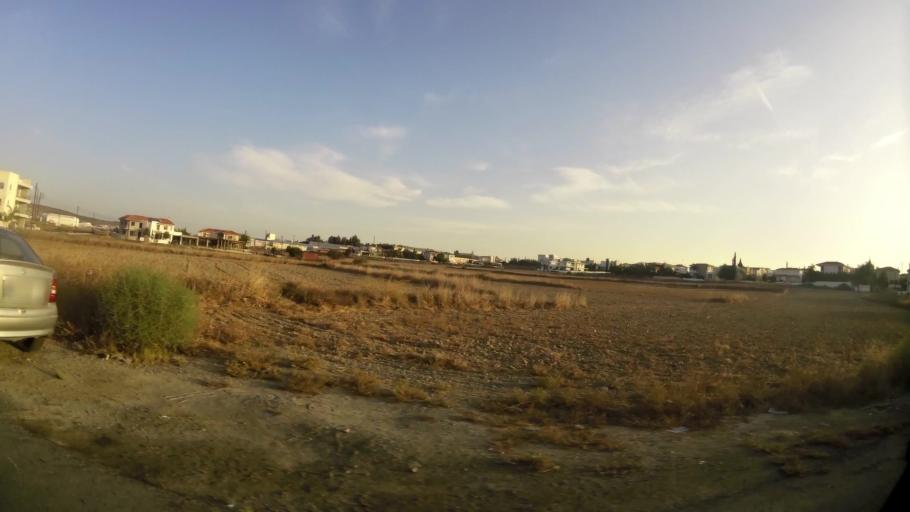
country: CY
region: Larnaka
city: Aradippou
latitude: 34.9254
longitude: 33.5862
